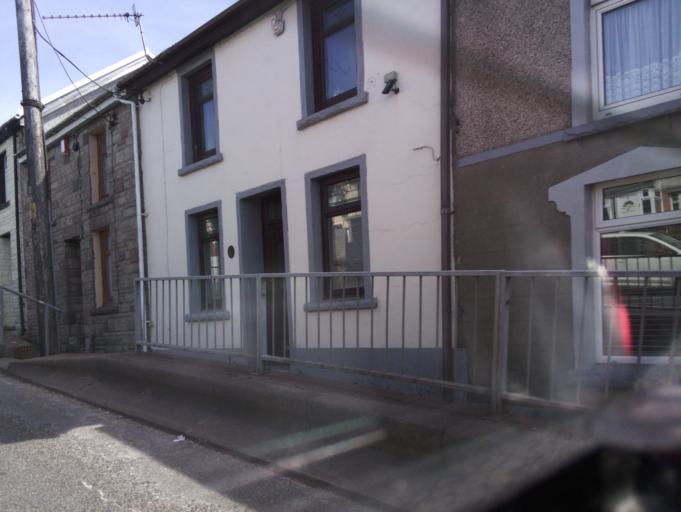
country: GB
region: Wales
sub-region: Merthyr Tydfil County Borough
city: Merthyr Tydfil
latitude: 51.7635
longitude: -3.3423
